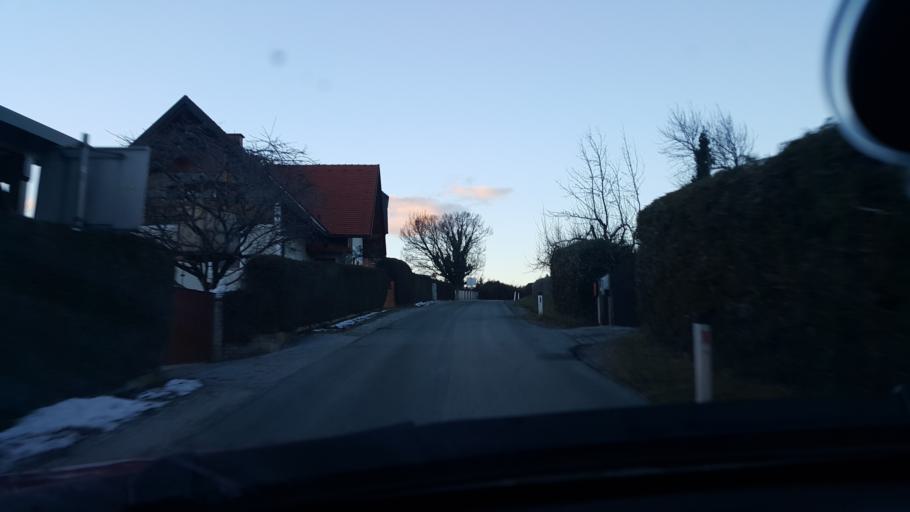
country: AT
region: Styria
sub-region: Politischer Bezirk Graz-Umgebung
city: Stiwoll
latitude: 47.1112
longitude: 15.2216
